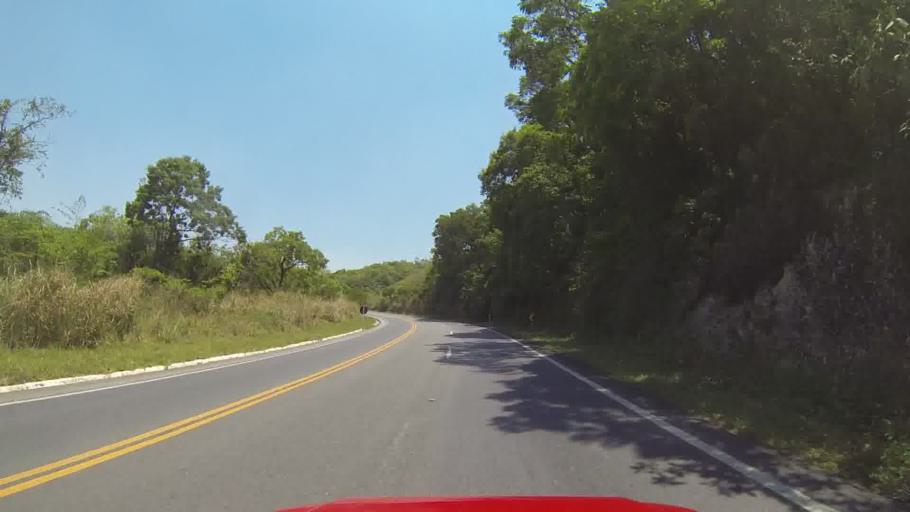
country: BR
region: Minas Gerais
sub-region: Itapecerica
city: Itapecerica
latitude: -20.2967
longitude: -45.1900
